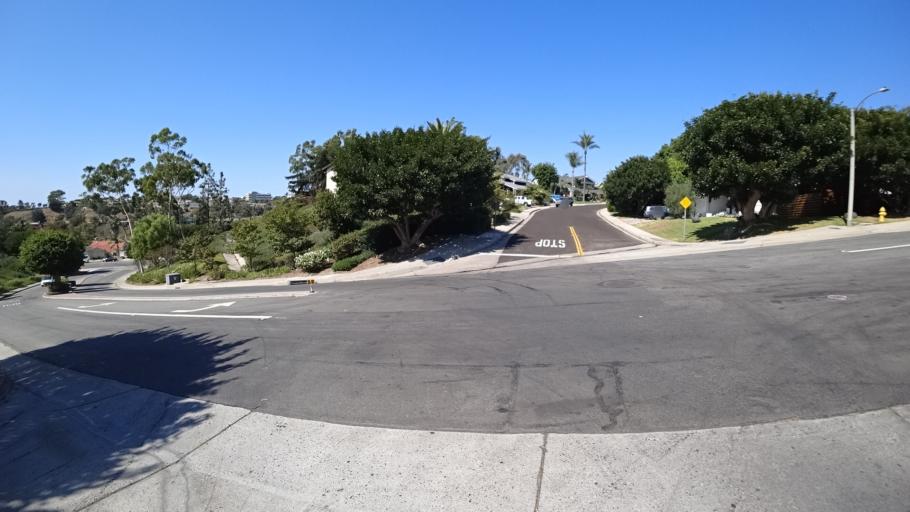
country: US
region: California
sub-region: Orange County
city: San Clemente
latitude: 33.4542
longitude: -117.6407
